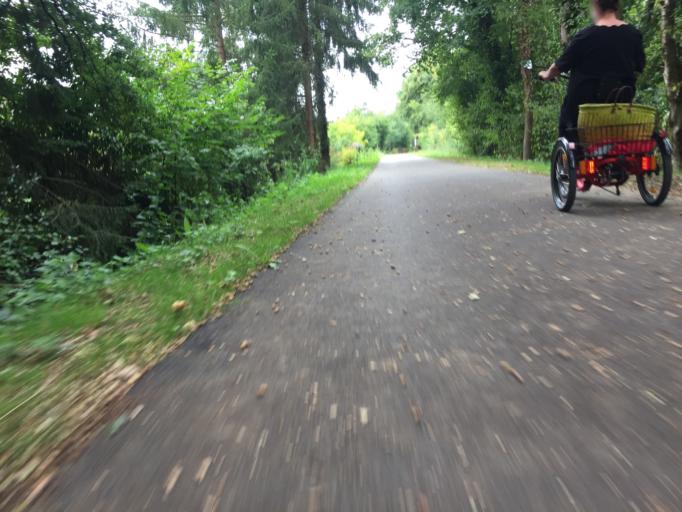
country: FR
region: Picardie
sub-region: Departement de l'Oise
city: Saint-Paul
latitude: 49.4015
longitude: 2.0104
